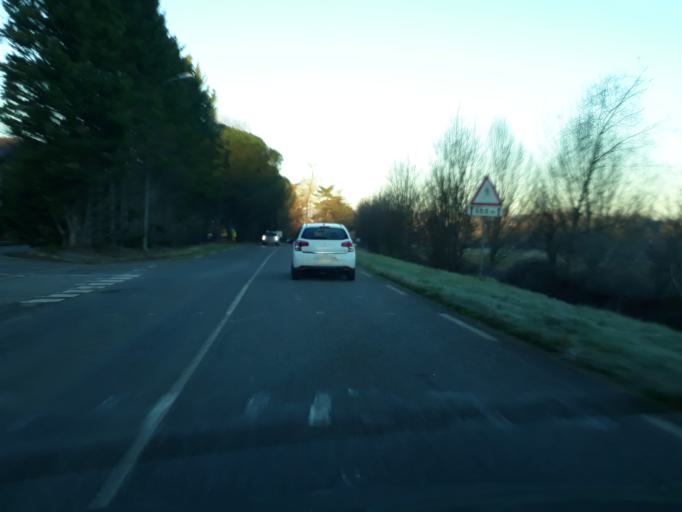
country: FR
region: Midi-Pyrenees
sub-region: Departement du Gers
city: Auch
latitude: 43.6357
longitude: 0.6071
